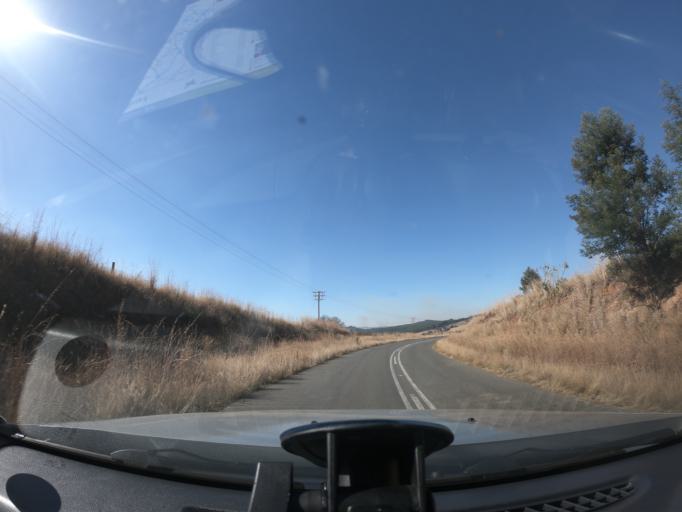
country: ZA
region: KwaZulu-Natal
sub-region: uMgungundlovu District Municipality
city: Howick
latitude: -29.4120
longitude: 30.0868
